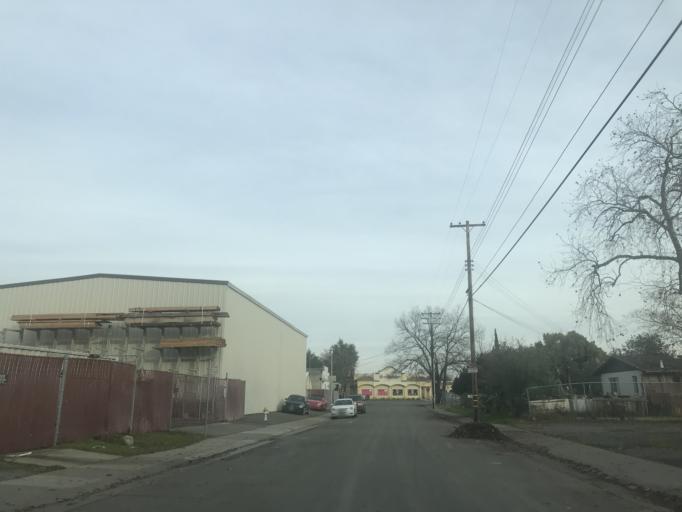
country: US
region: California
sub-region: Sacramento County
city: Parkway
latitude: 38.5266
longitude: -121.4737
